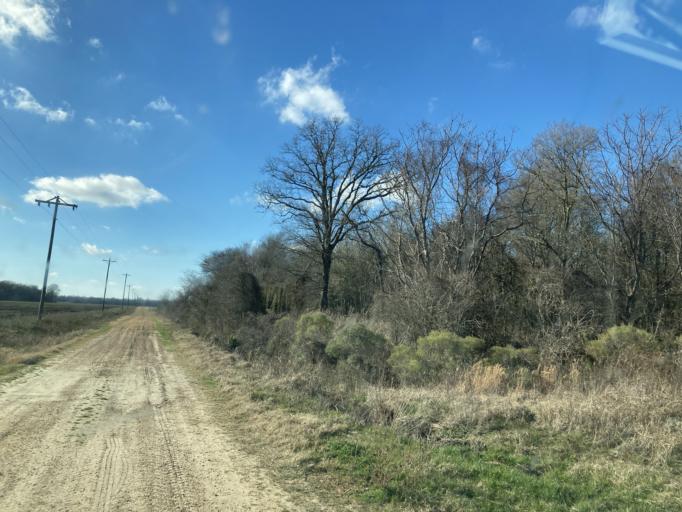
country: US
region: Mississippi
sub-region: Yazoo County
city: Yazoo City
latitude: 32.9479
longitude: -90.5090
